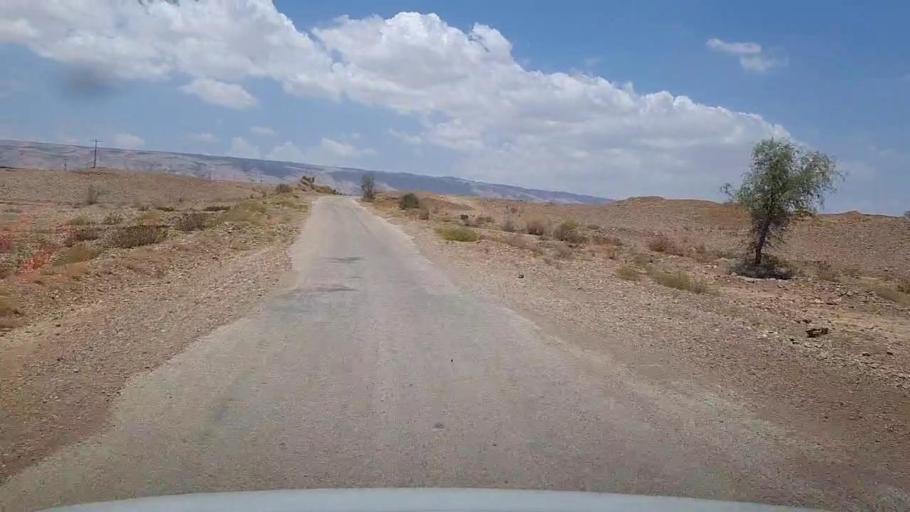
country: PK
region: Sindh
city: Bhan
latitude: 26.3200
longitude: 67.5529
